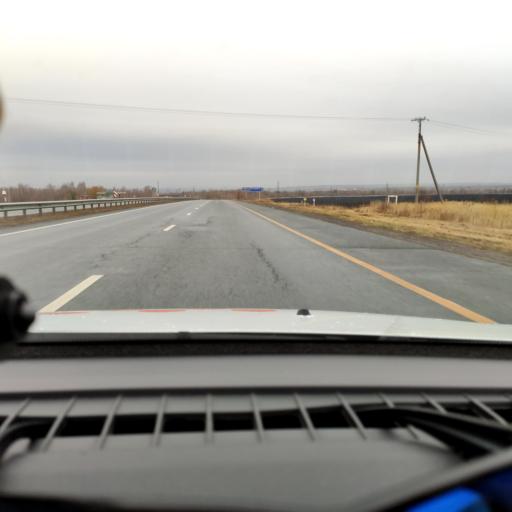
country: RU
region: Samara
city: Novokuybyshevsk
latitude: 53.0135
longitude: 49.9789
